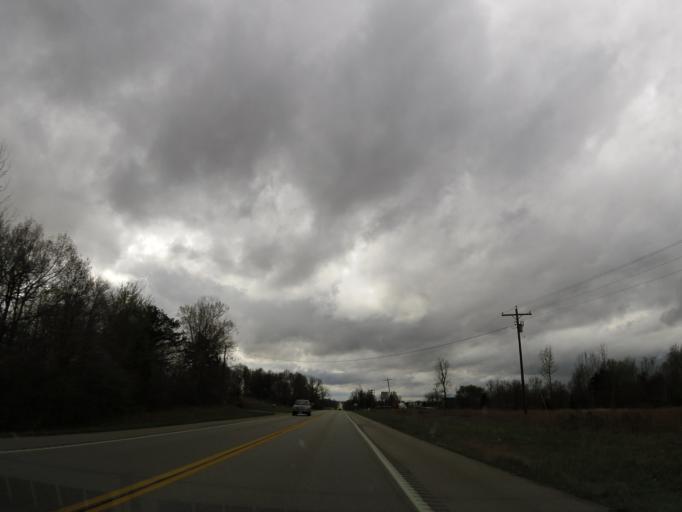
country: US
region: Missouri
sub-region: Butler County
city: Poplar Bluff
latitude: 36.6522
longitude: -90.5201
